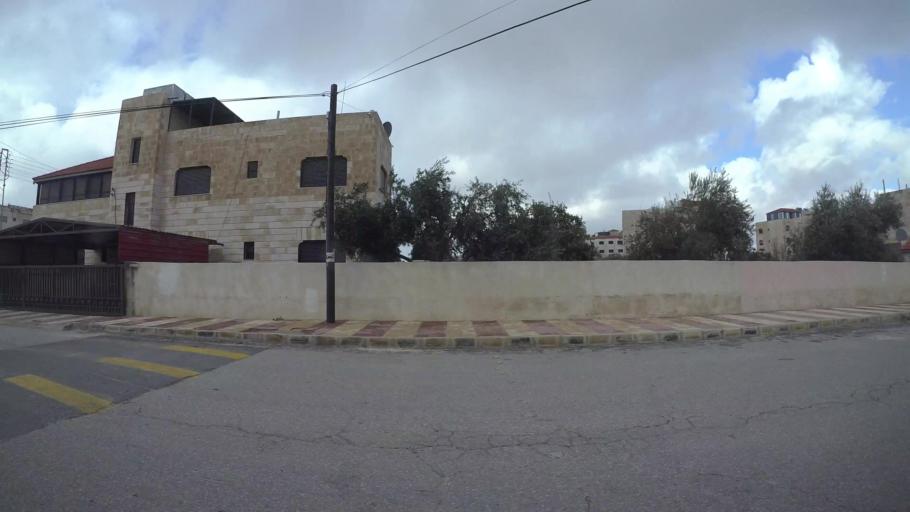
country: JO
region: Amman
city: Al Jubayhah
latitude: 32.0445
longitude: 35.9008
